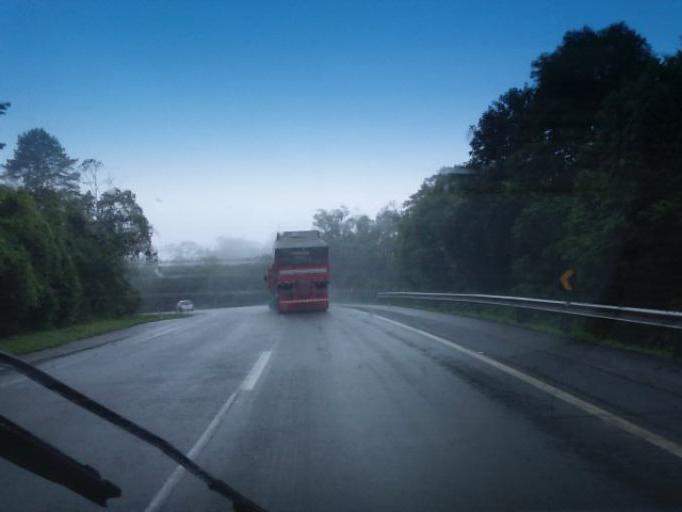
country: BR
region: Parana
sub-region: Antonina
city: Antonina
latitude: -25.1123
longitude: -48.7681
